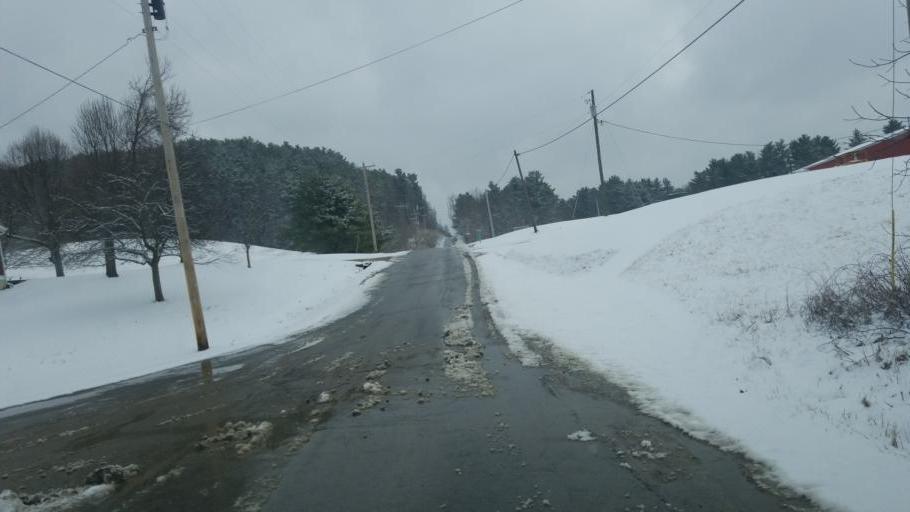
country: US
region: Ohio
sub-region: Knox County
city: Danville
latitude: 40.4610
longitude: -82.2175
